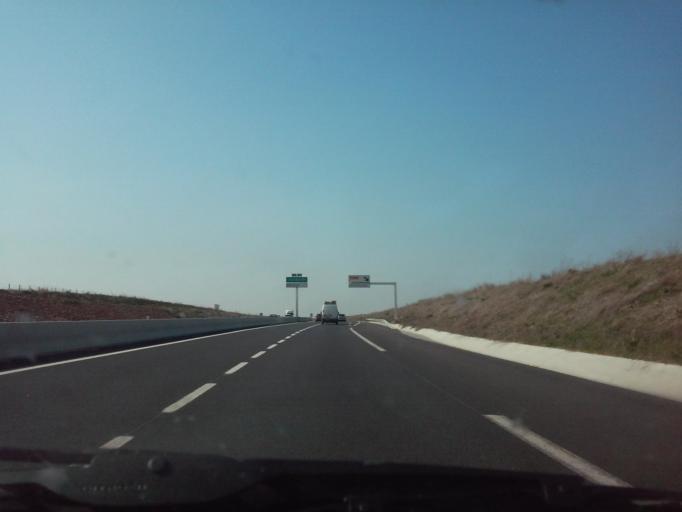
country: FR
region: Lower Normandy
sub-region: Departement du Calvados
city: Creully
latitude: 49.2290
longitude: -0.5715
